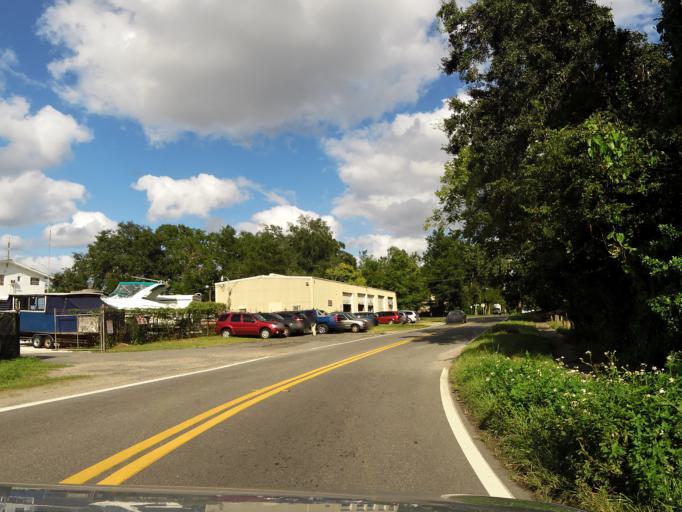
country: US
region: Florida
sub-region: Duval County
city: Jacksonville
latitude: 30.2812
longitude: -81.7393
